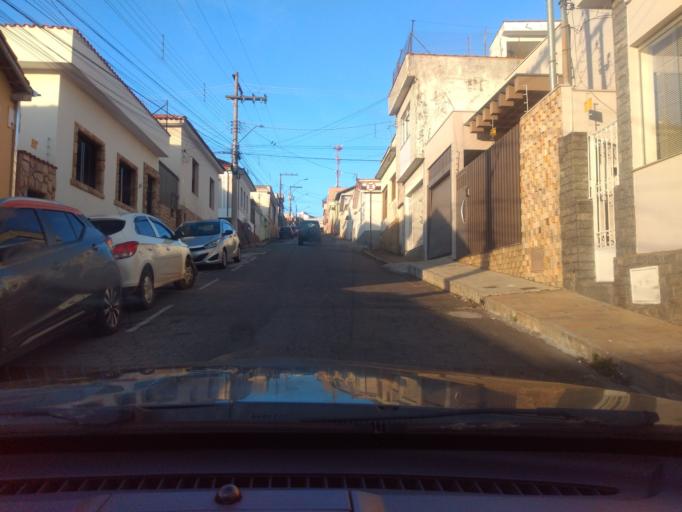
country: BR
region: Minas Gerais
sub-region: Tres Coracoes
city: Tres Coracoes
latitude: -21.6963
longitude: -45.2516
